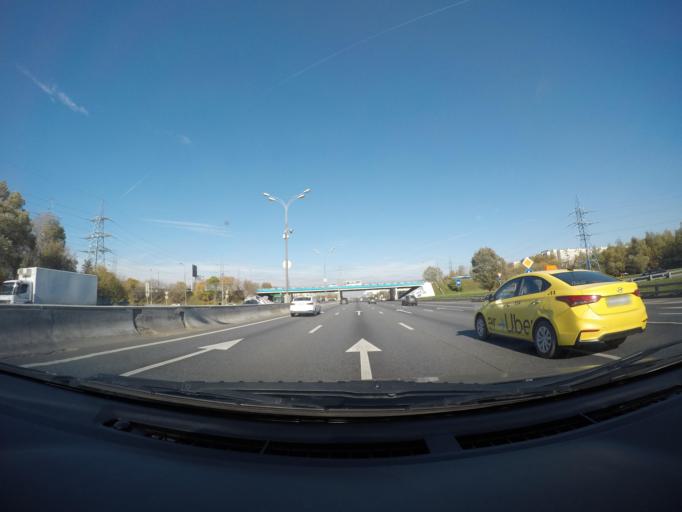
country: RU
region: Moskovskaya
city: Kuskovo
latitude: 55.7428
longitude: 37.8419
